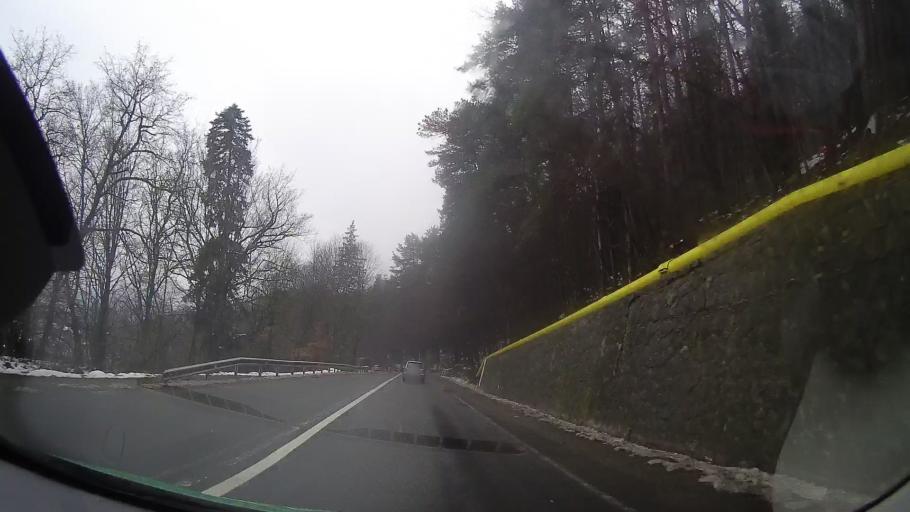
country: RO
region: Neamt
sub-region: Comuna Tarcau
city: Tarcau
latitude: 46.8946
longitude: 26.1232
